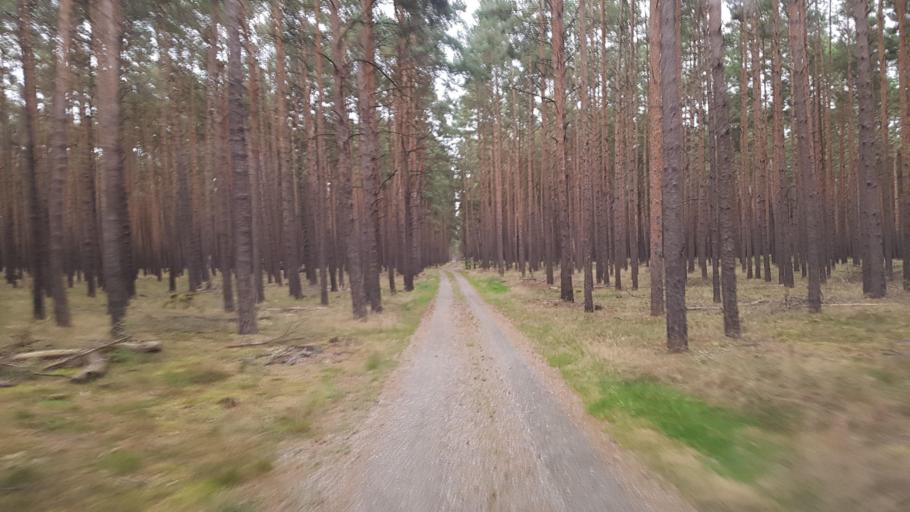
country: DE
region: Brandenburg
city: Sonnewalde
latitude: 51.7378
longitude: 13.6576
